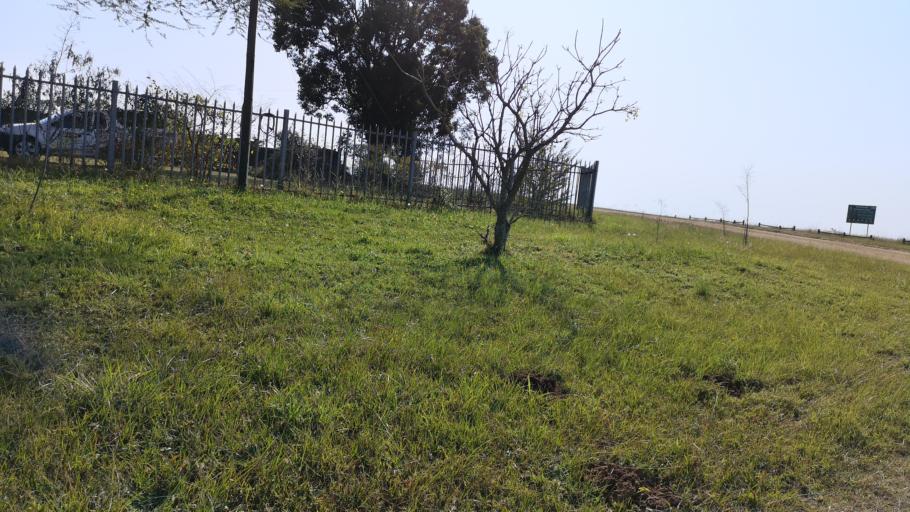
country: ZA
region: KwaZulu-Natal
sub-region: eThekwini Metropolitan Municipality
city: Mpumalanga
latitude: -29.7360
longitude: 30.6856
